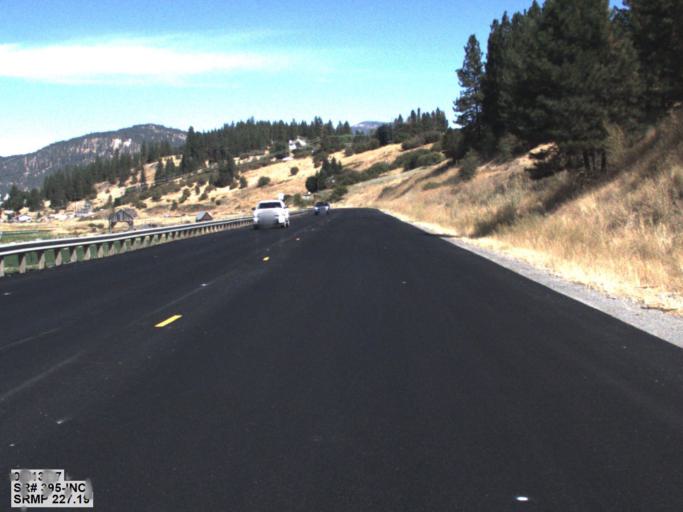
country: US
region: Washington
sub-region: Stevens County
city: Colville
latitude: 48.5111
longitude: -117.9009
